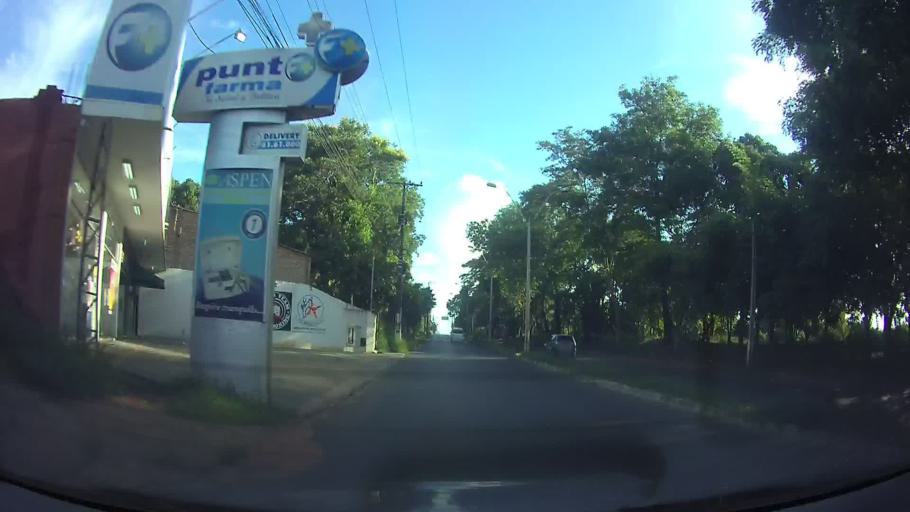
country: PY
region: Central
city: Villa Elisa
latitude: -25.3723
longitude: -57.5843
